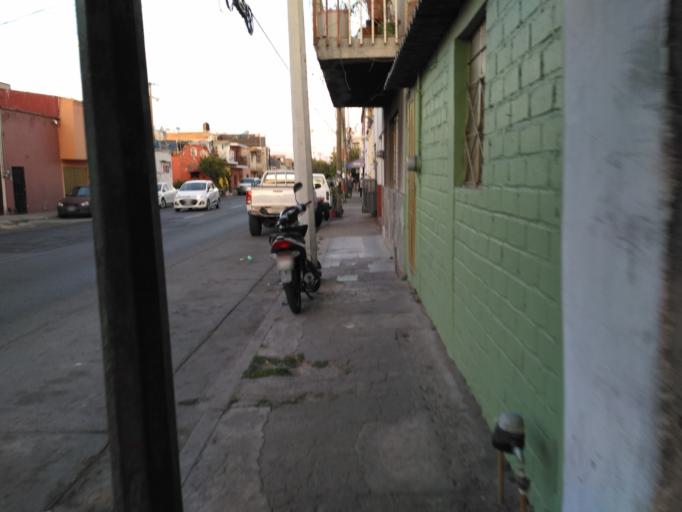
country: MX
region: Jalisco
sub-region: Zapopan
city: Zapopan
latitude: 20.6933
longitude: -103.3624
